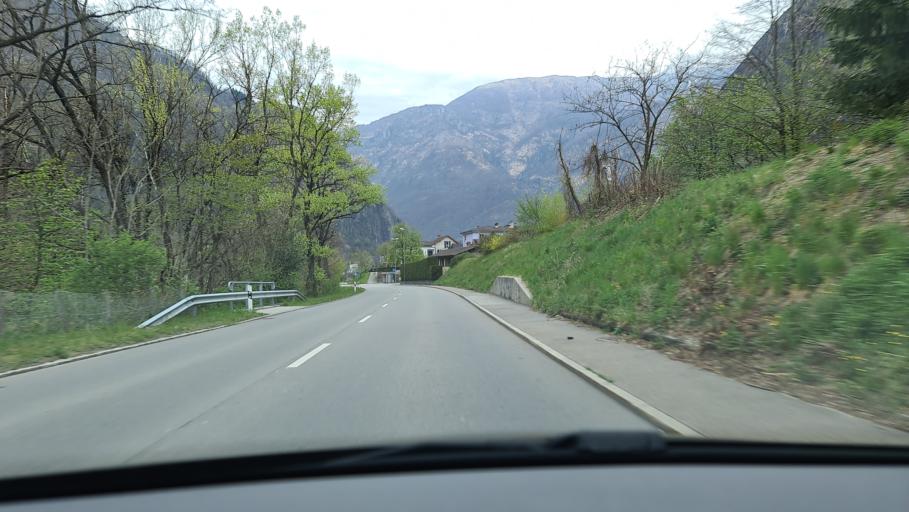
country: CH
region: Ticino
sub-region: Locarno District
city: Verscio
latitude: 46.2042
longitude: 8.7431
